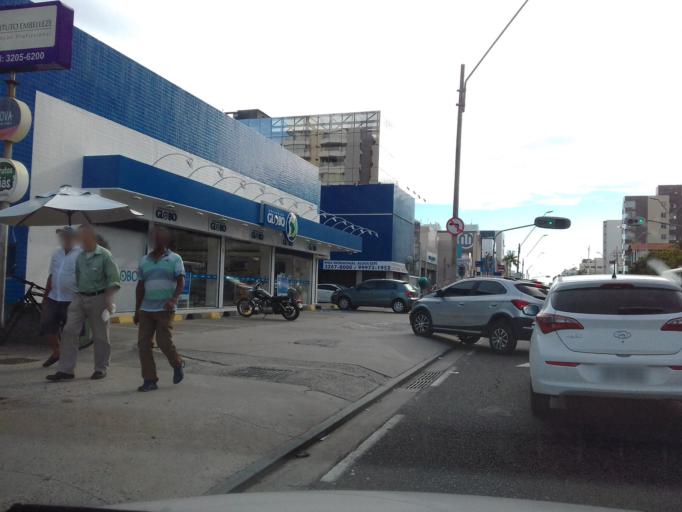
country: BR
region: Bahia
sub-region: Salvador
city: Salvador
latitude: -13.0077
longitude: -38.4628
